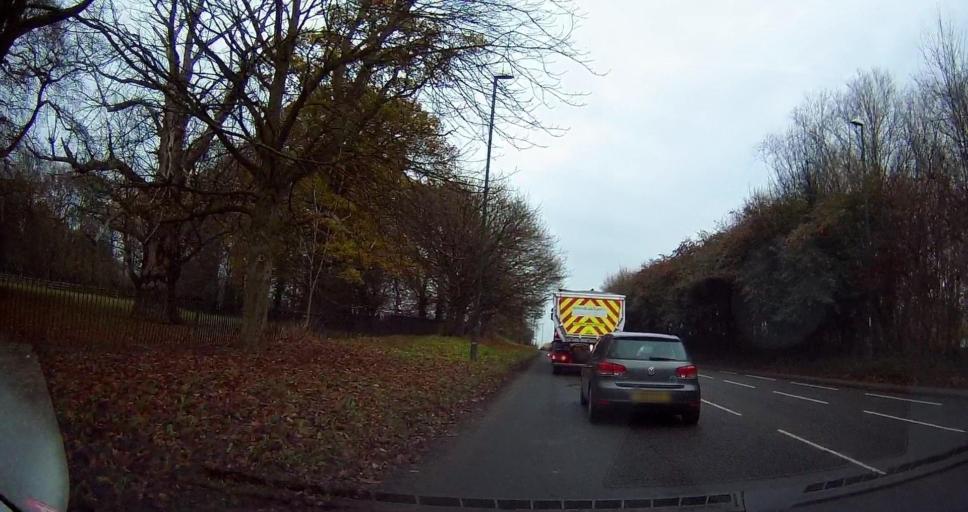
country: GB
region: England
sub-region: Nottinghamshire
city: Kimberley
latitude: 52.9732
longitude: -1.2340
